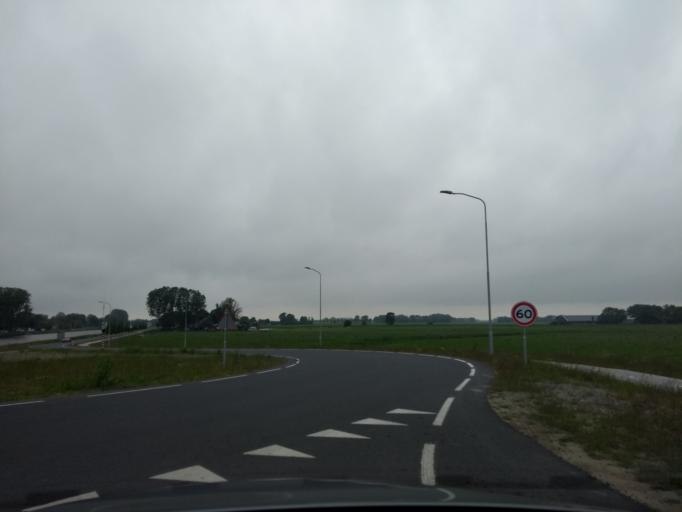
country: NL
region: Groningen
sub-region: Gemeente Zuidhorn
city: Aduard
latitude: 53.2612
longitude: 6.4692
